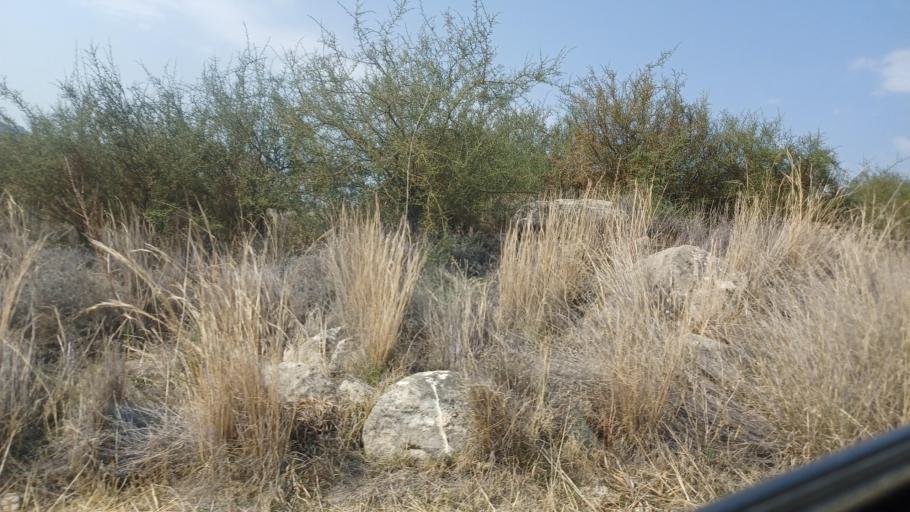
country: CY
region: Pafos
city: Polis
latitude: 34.9867
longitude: 32.4579
